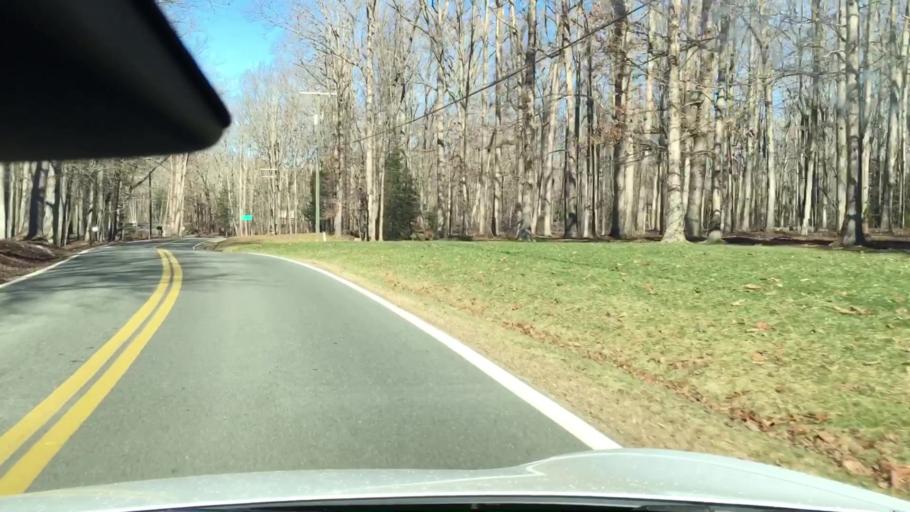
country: US
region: Virginia
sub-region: Powhatan County
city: Powhatan
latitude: 37.5590
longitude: -77.7990
